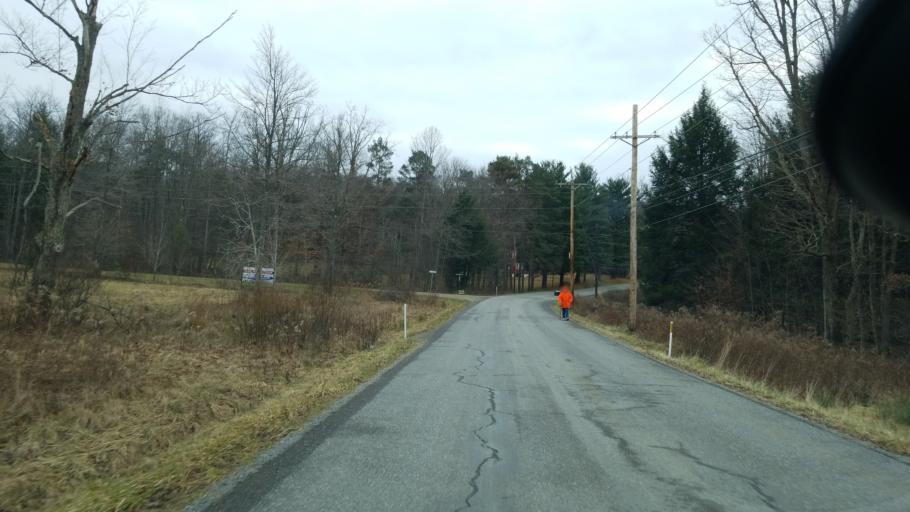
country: US
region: Pennsylvania
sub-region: Clearfield County
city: Treasure Lake
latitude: 41.1151
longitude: -78.6911
